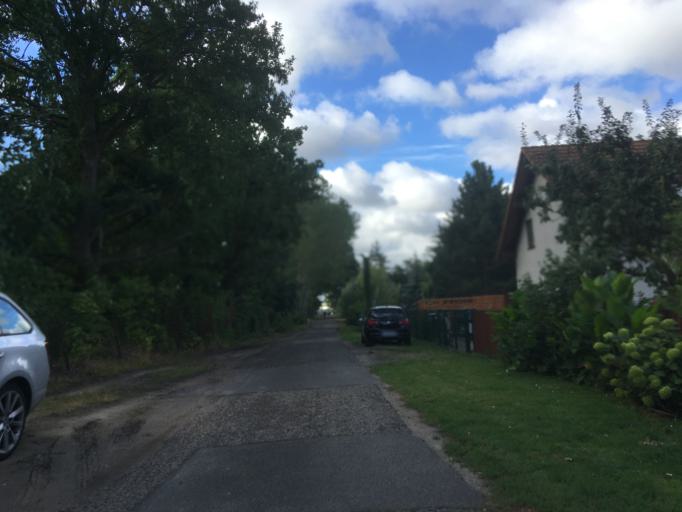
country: DE
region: Berlin
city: Neu-Hohenschoenhausen
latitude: 52.5534
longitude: 13.5239
